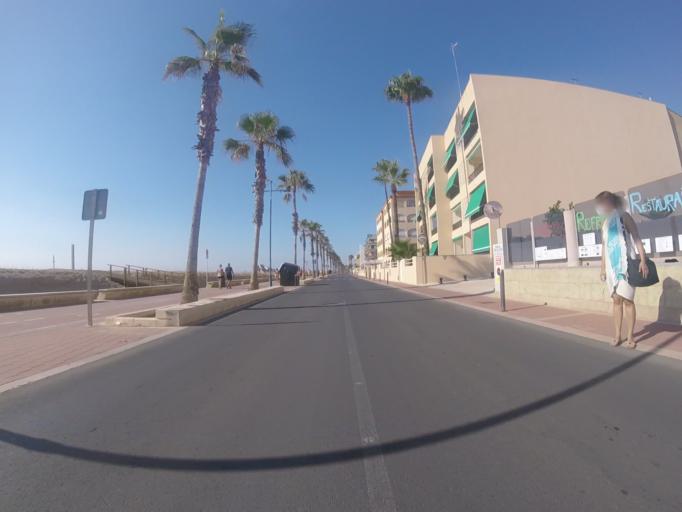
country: ES
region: Valencia
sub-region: Provincia de Castello
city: Peniscola
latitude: 40.3776
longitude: 0.4073
